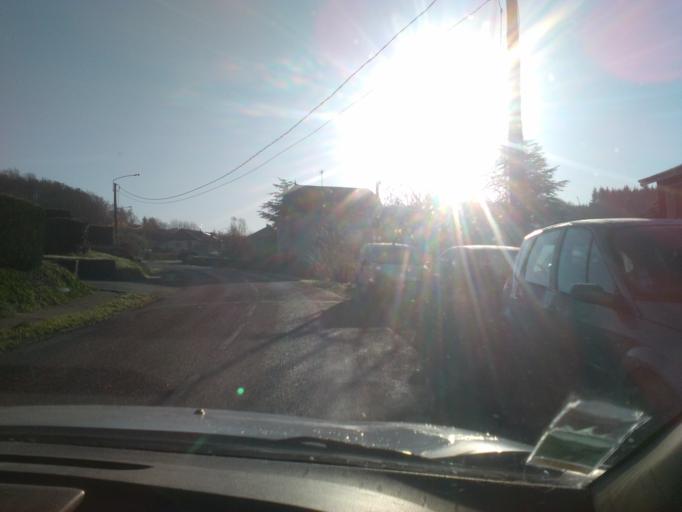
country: FR
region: Lorraine
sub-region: Departement des Vosges
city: Xertigny
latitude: 48.0531
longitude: 6.3740
